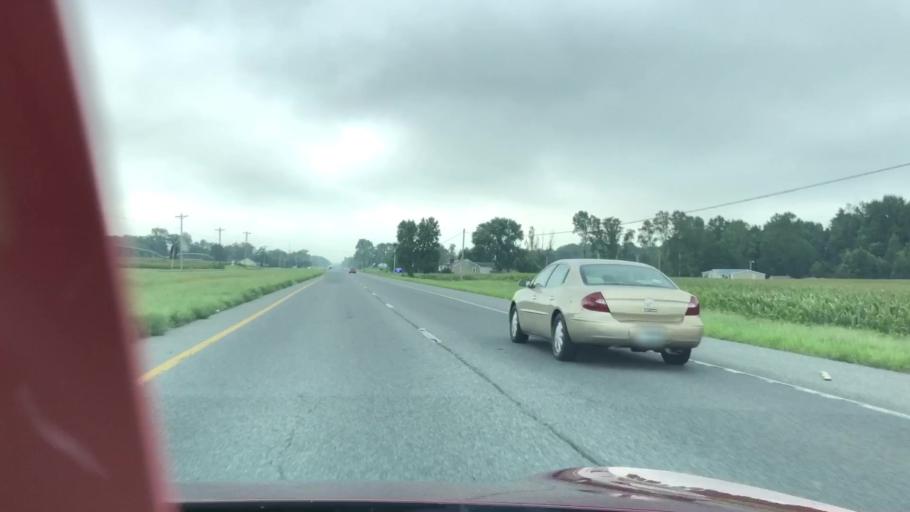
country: US
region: Delaware
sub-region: Sussex County
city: Bridgeville
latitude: 38.7881
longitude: -75.5911
